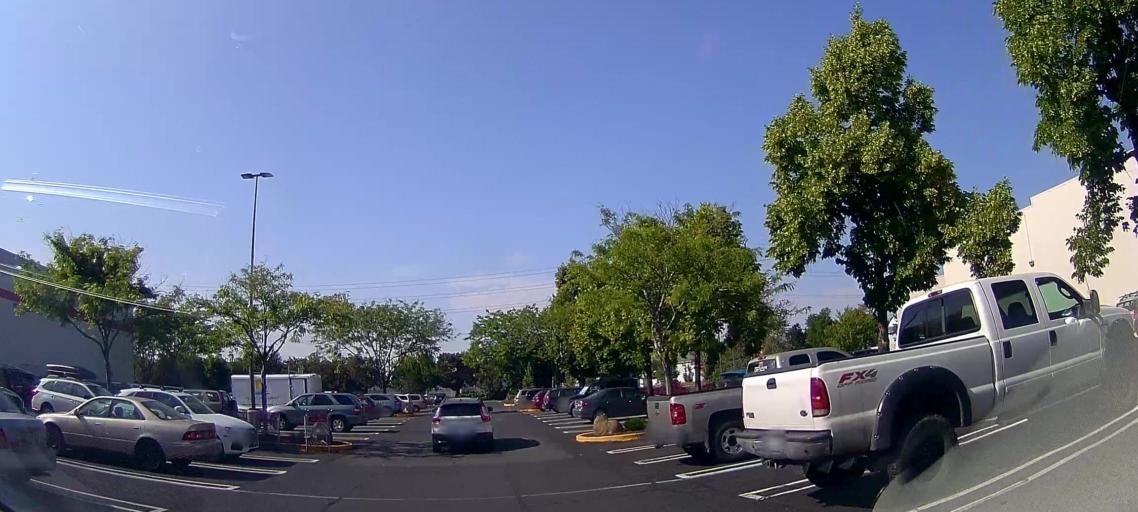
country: US
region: Oregon
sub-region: Deschutes County
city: Bend
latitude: 44.0576
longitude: -121.2666
